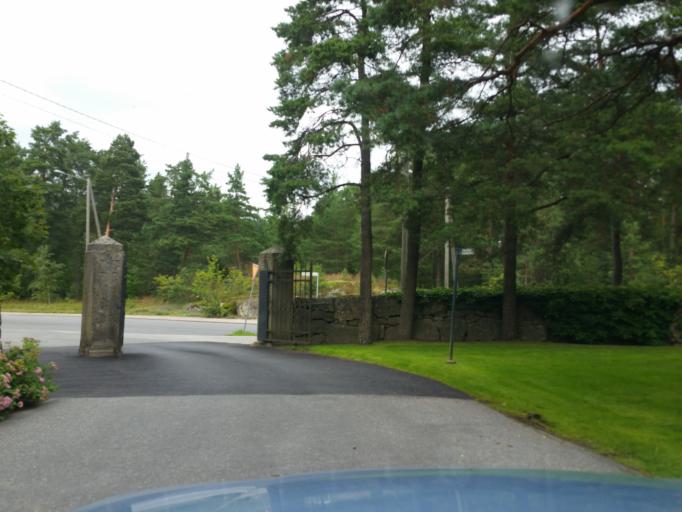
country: FI
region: Varsinais-Suomi
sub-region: Turku
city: Turku
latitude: 60.4350
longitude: 22.3119
